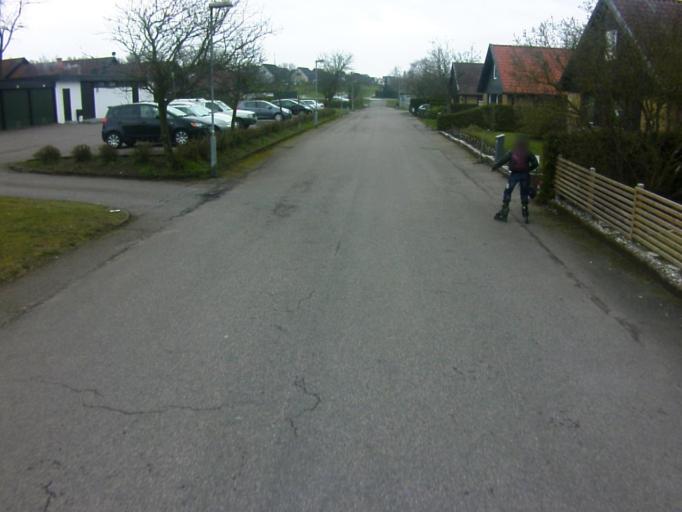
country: SE
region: Skane
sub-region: Kavlinge Kommun
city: Kaevlinge
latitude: 55.7715
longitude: 13.0874
